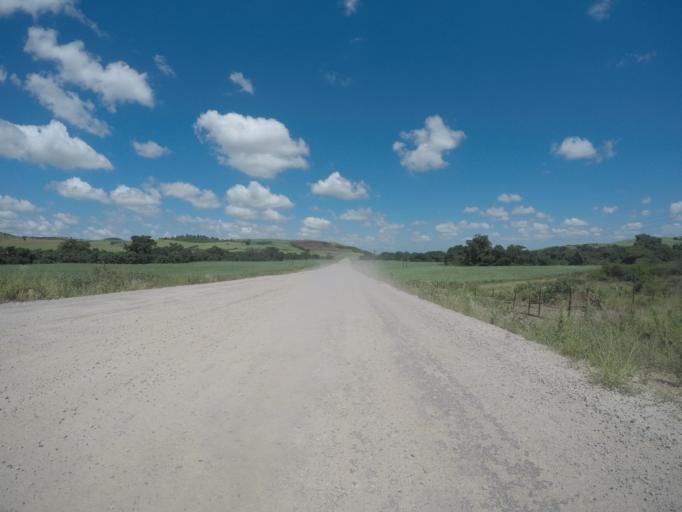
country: ZA
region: KwaZulu-Natal
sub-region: uThungulu District Municipality
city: Empangeni
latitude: -28.6417
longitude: 31.7649
